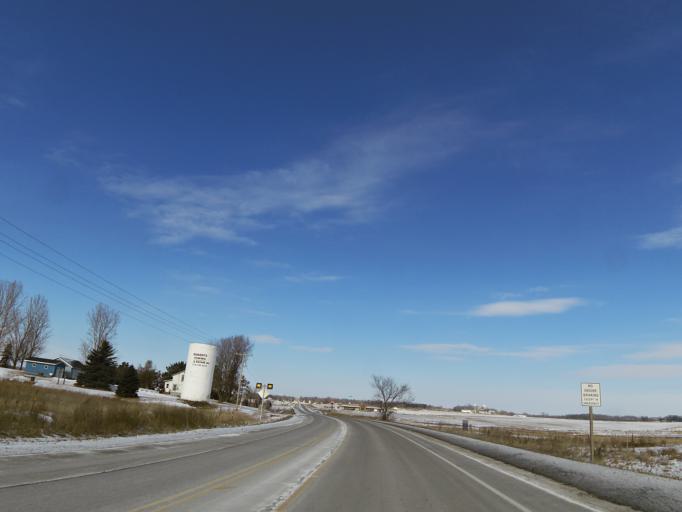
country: US
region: Wisconsin
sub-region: Saint Croix County
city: Roberts
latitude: 44.9650
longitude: -92.5582
